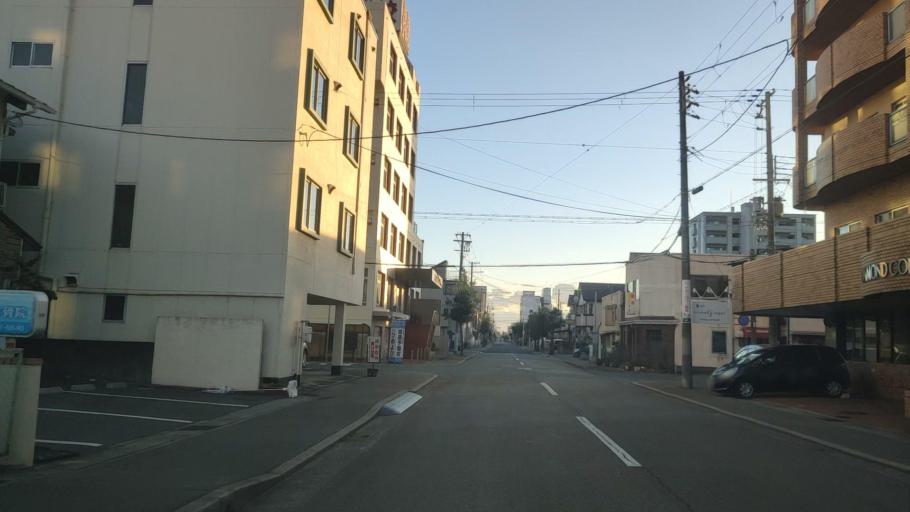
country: JP
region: Hyogo
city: Himeji
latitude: 34.8249
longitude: 134.6852
